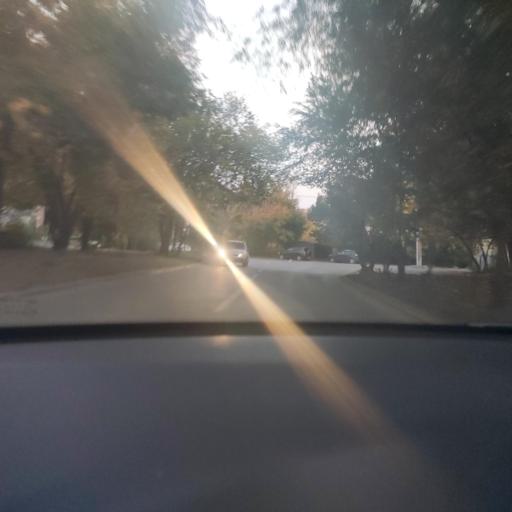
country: RU
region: Samara
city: Samara
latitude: 53.2151
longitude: 50.2004
